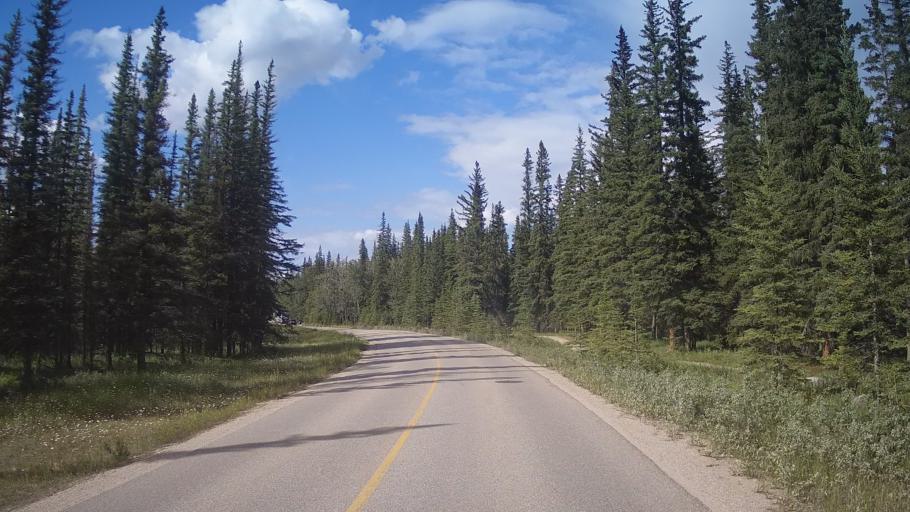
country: CA
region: Alberta
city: Jasper Park Lodge
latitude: 52.8625
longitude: -118.0704
